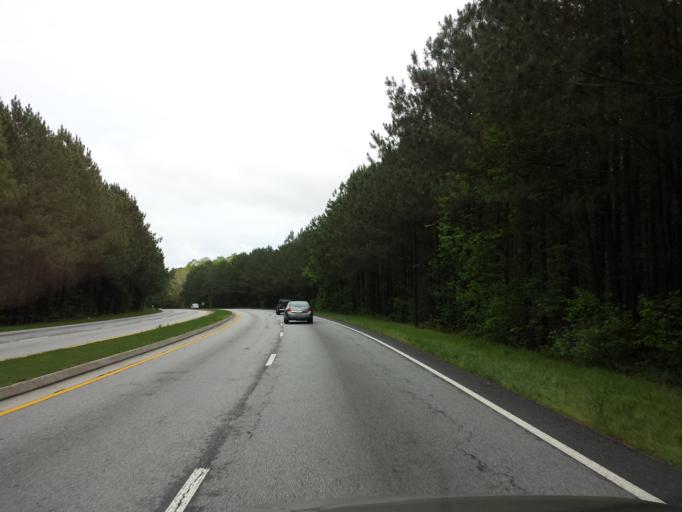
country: US
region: Georgia
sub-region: Cobb County
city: Mableton
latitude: 33.8452
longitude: -84.5461
